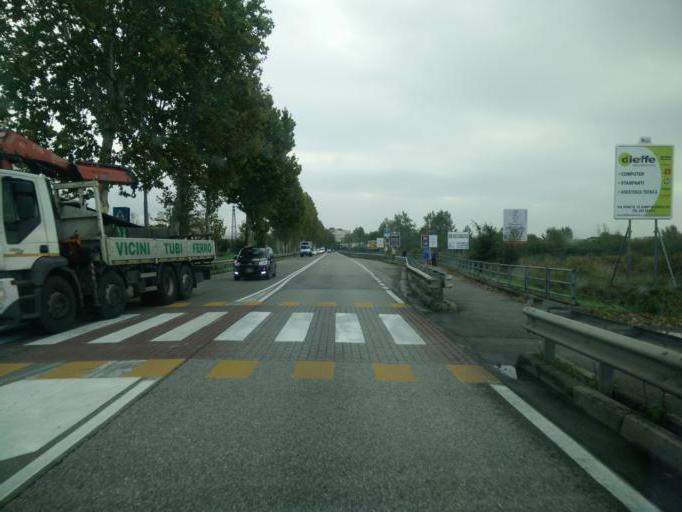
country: IT
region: Tuscany
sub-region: Province of Florence
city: San Donnino
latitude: 43.8106
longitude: 11.1649
